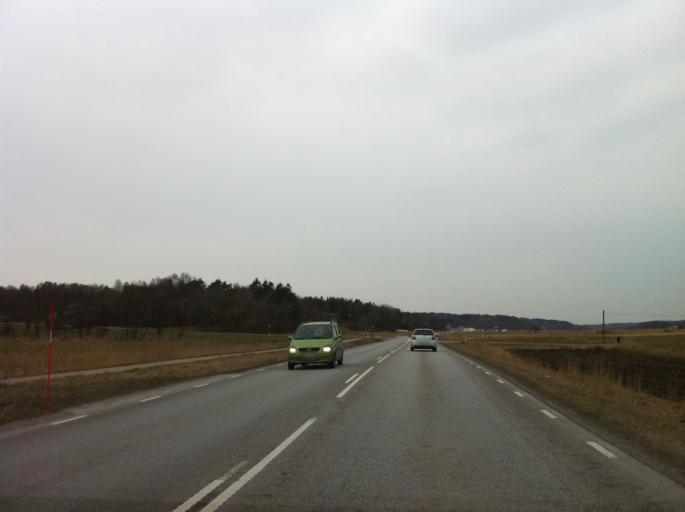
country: SE
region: Vaestra Goetaland
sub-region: Orust
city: Henan
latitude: 58.2190
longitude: 11.6892
